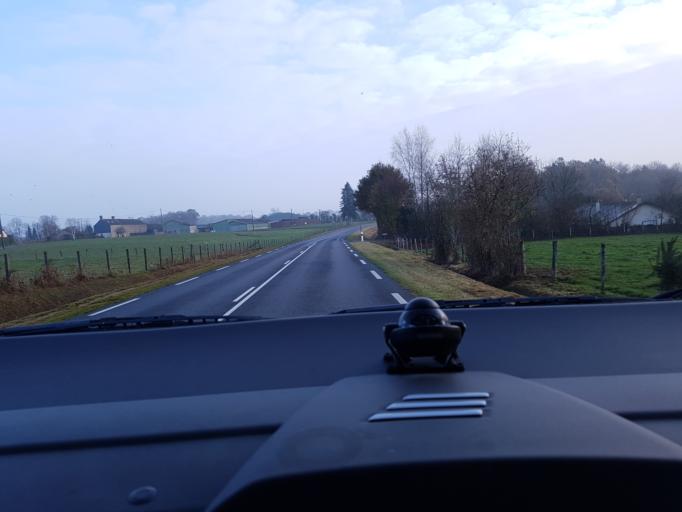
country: FR
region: Lower Normandy
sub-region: Departement de l'Orne
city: Magny-le-Desert
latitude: 48.6172
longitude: -0.3009
